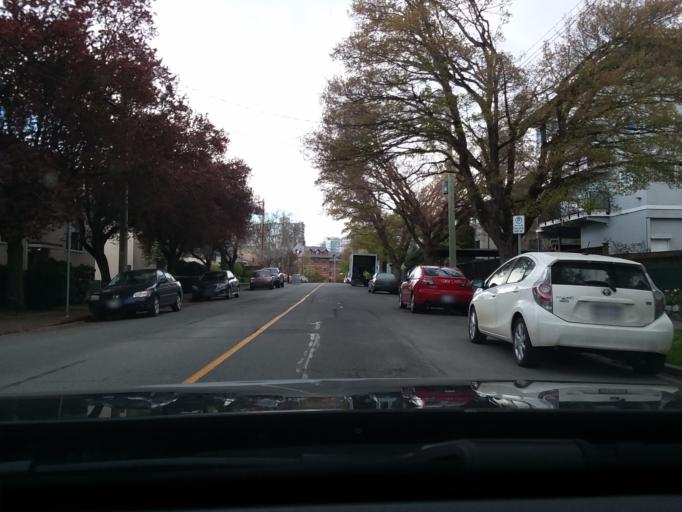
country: CA
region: British Columbia
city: Victoria
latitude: 48.4185
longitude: -123.3587
